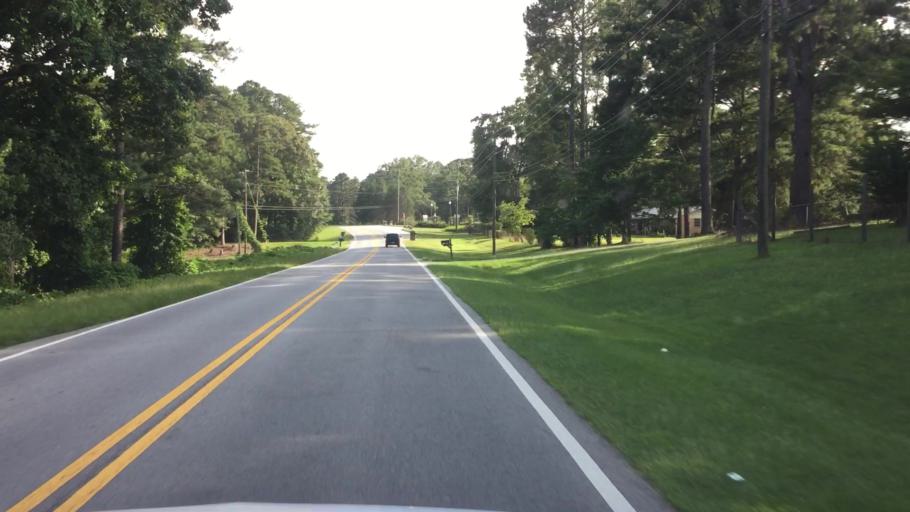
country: US
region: Georgia
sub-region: DeKalb County
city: Pine Mountain
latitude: 33.6151
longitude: -84.1353
